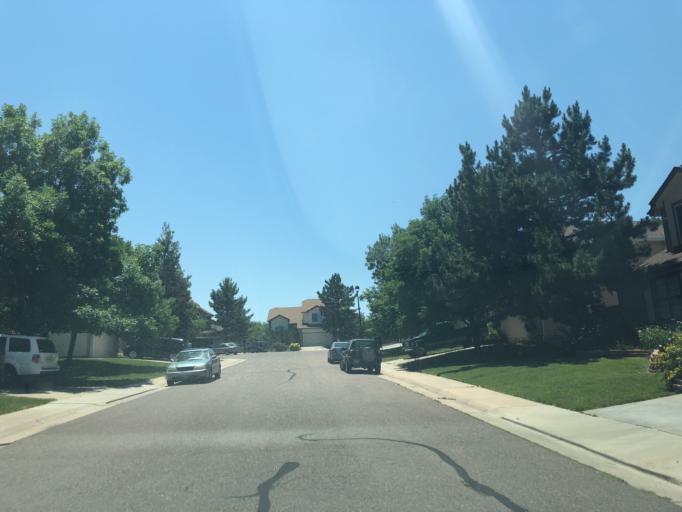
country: US
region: Colorado
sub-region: Arapahoe County
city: Dove Valley
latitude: 39.6178
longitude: -104.7557
